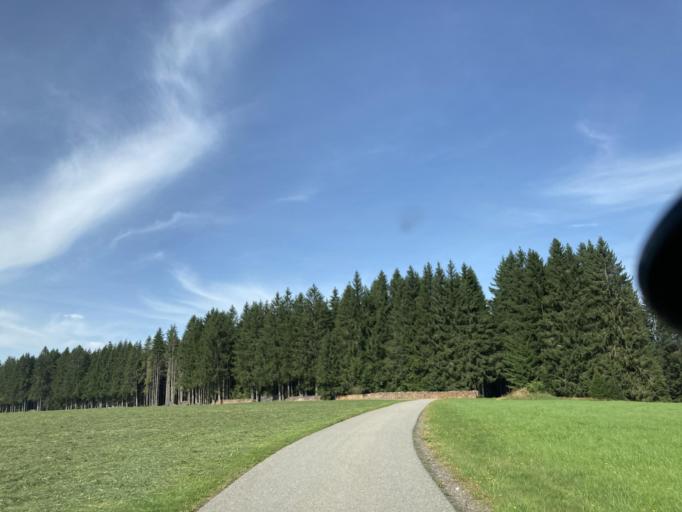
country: DE
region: Baden-Wuerttemberg
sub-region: Freiburg Region
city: Schonwald im Schwarzwald
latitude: 48.0876
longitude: 8.2187
